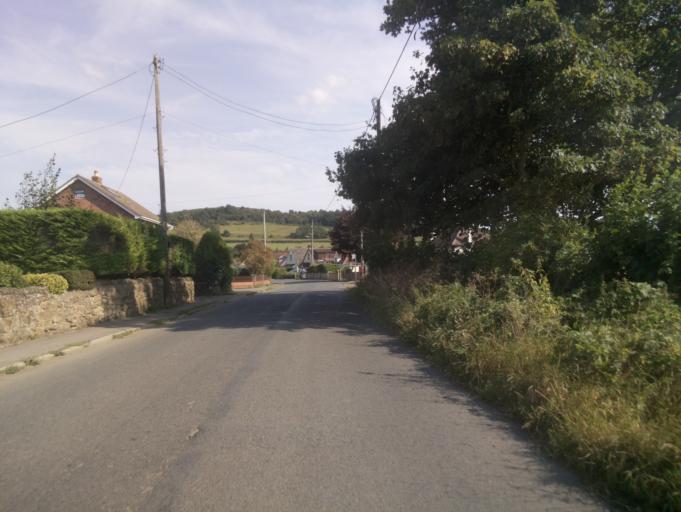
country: GB
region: England
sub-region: Gloucestershire
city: Dursley
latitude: 51.6987
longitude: -2.3424
